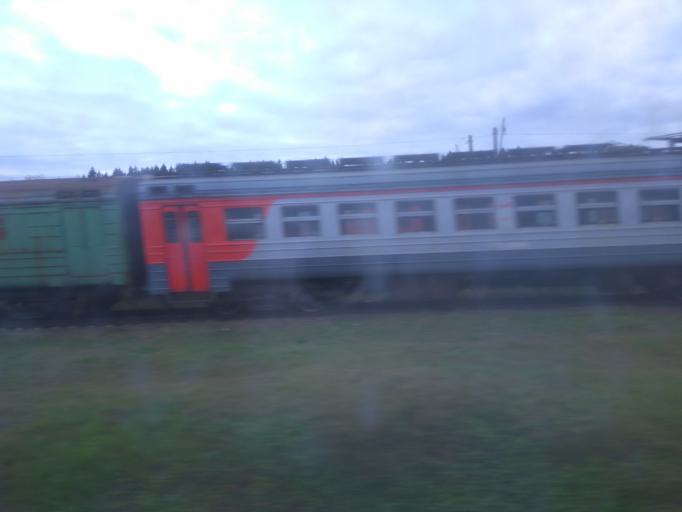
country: RU
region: Moskovskaya
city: Aprelevka
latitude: 55.5598
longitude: 37.0884
